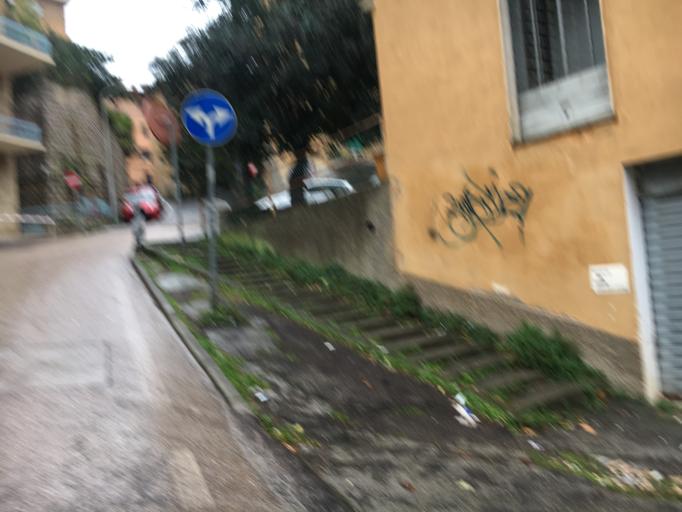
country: IT
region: Umbria
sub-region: Provincia di Perugia
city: Perugia
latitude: 43.1132
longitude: 12.3803
